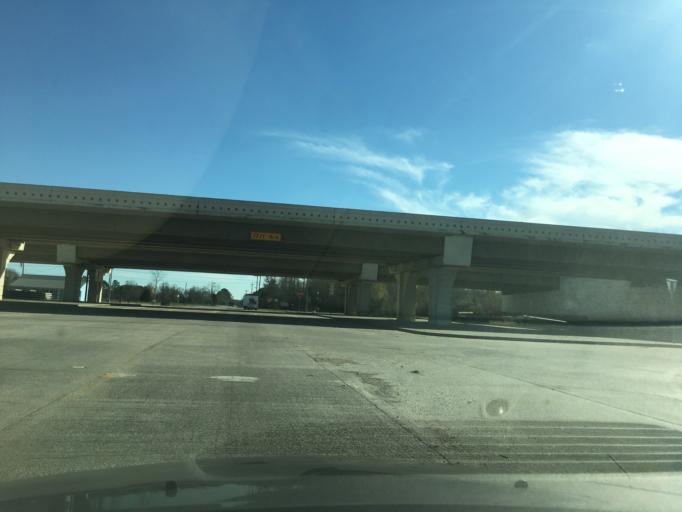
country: US
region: Texas
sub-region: Wharton County
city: East Bernard
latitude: 29.4468
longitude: -96.0000
